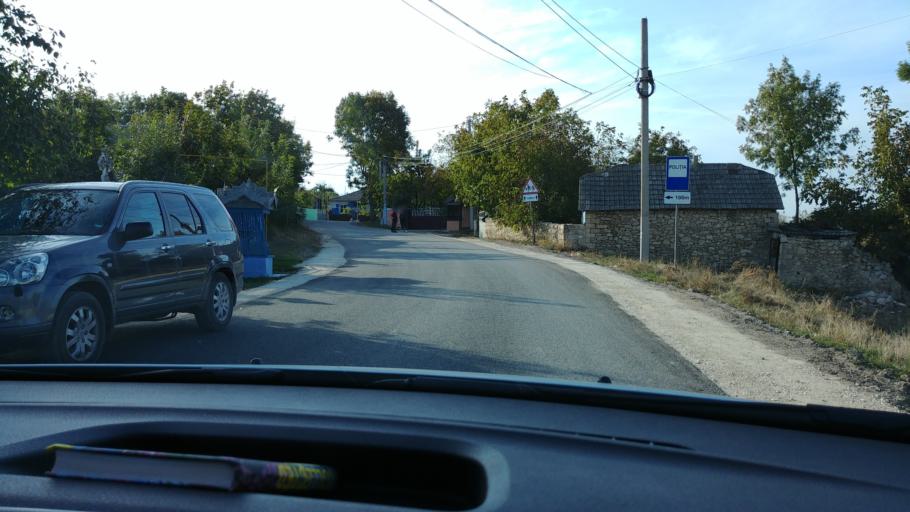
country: MD
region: Rezina
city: Rezina
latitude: 47.7491
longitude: 28.8835
